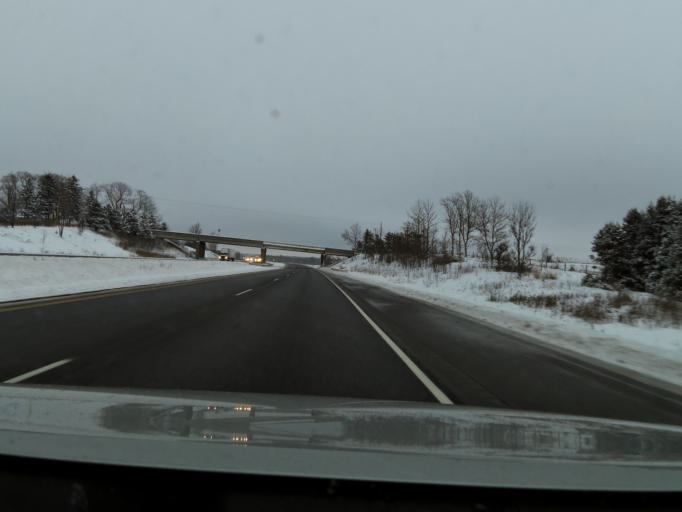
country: US
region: Wisconsin
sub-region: Saint Croix County
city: Woodville
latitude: 44.9361
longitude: -92.3209
